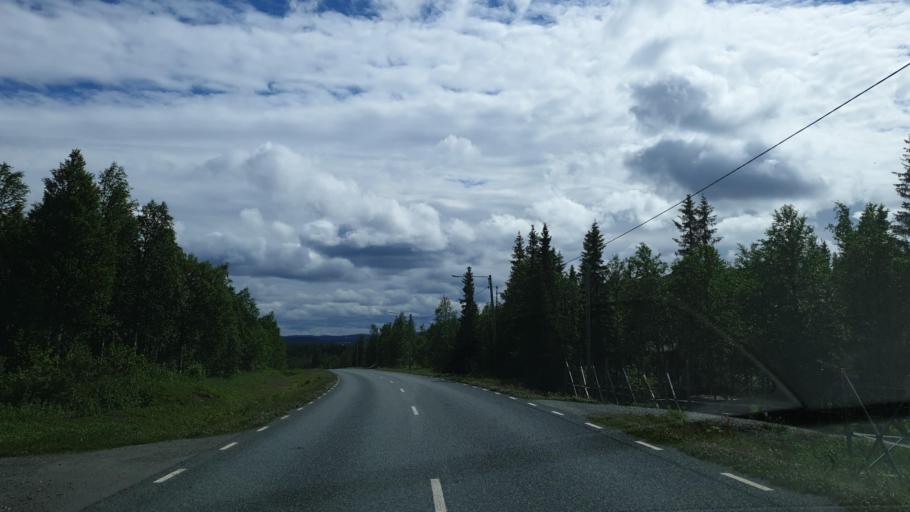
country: SE
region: Vaesterbotten
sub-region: Vilhelmina Kommun
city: Sjoberg
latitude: 65.2532
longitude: 15.5346
